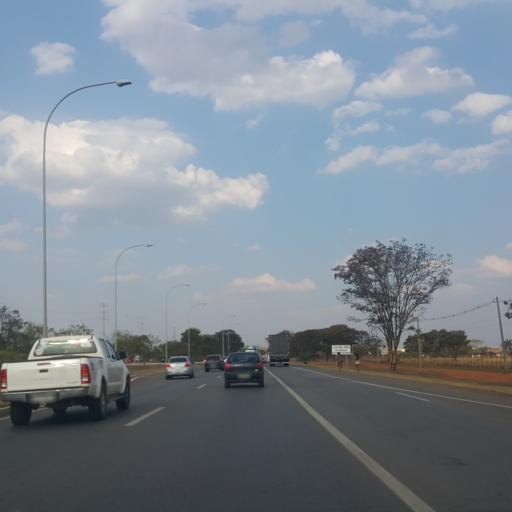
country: BR
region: Federal District
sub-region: Brasilia
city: Brasilia
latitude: -15.8755
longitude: -48.0330
